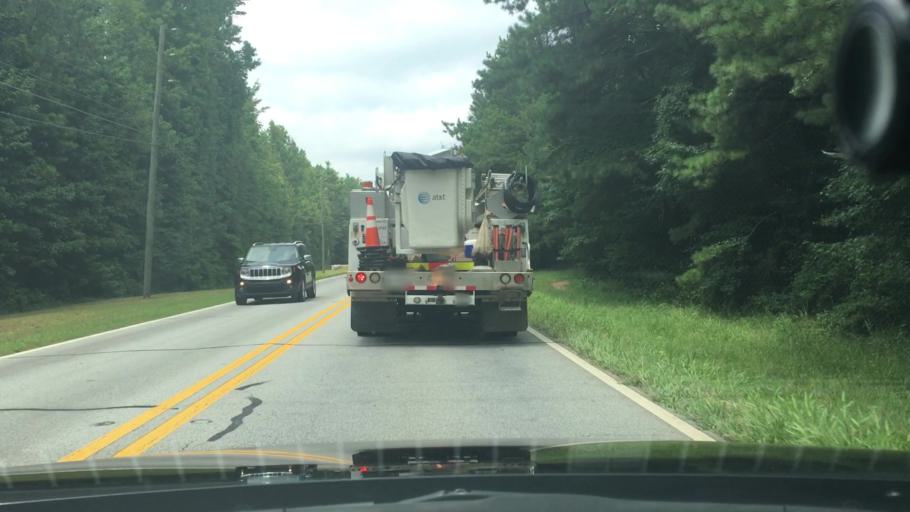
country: US
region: Georgia
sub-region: Coweta County
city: East Newnan
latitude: 33.3486
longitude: -84.6960
